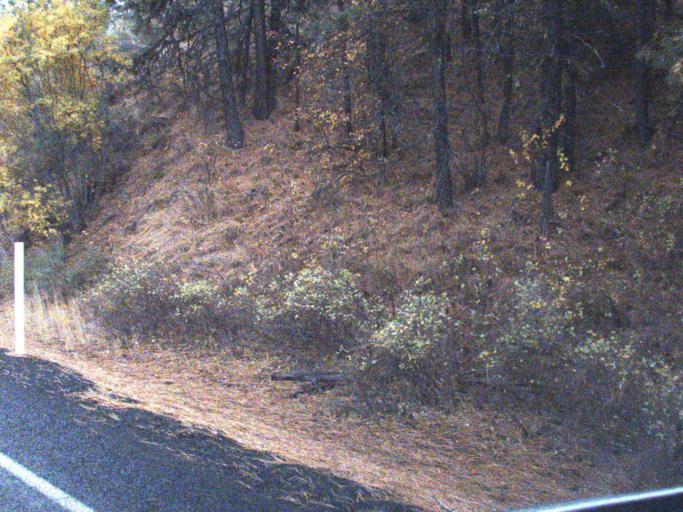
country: US
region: Washington
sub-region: Lincoln County
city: Davenport
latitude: 47.8229
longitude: -118.1850
